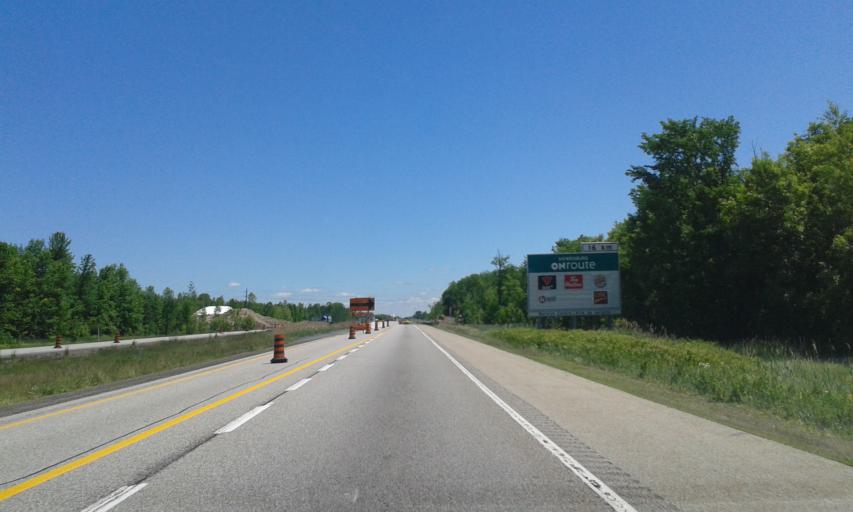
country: US
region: New York
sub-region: St. Lawrence County
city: Ogdensburg
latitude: 44.8682
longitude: -75.3094
